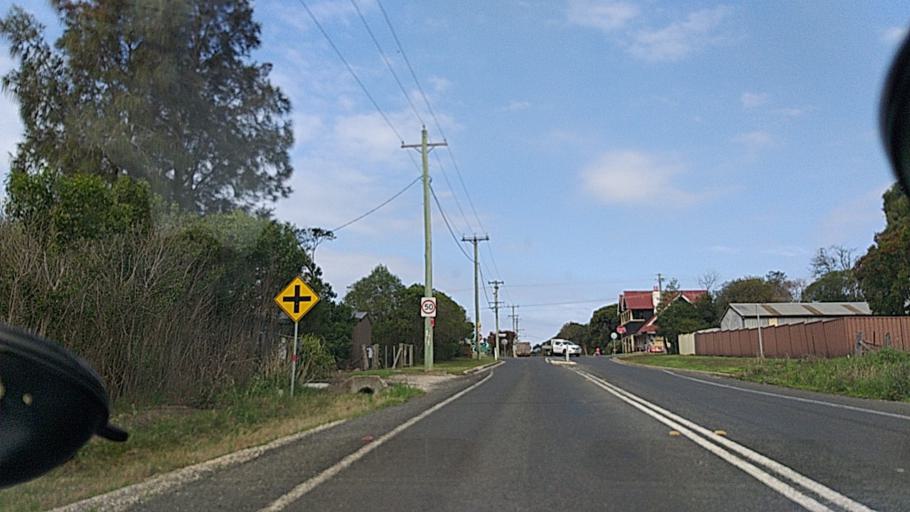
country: AU
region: New South Wales
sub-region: Camden
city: Camden South
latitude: -34.1269
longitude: 150.7376
